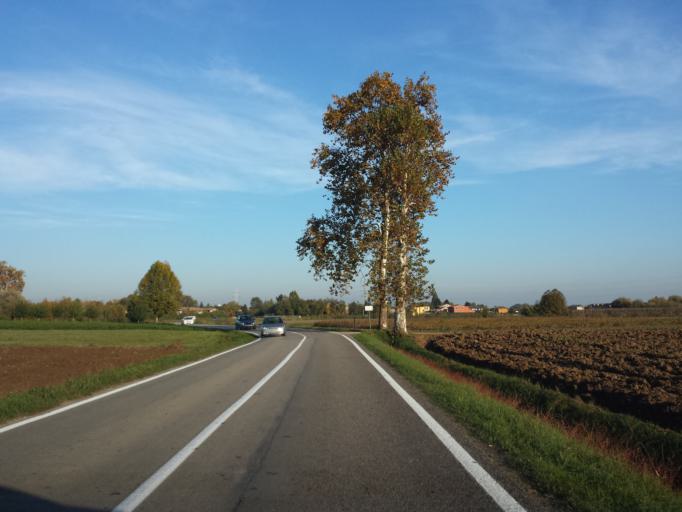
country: IT
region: Veneto
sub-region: Provincia di Vicenza
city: Crispi Cavour
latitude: 45.5897
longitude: 11.5097
